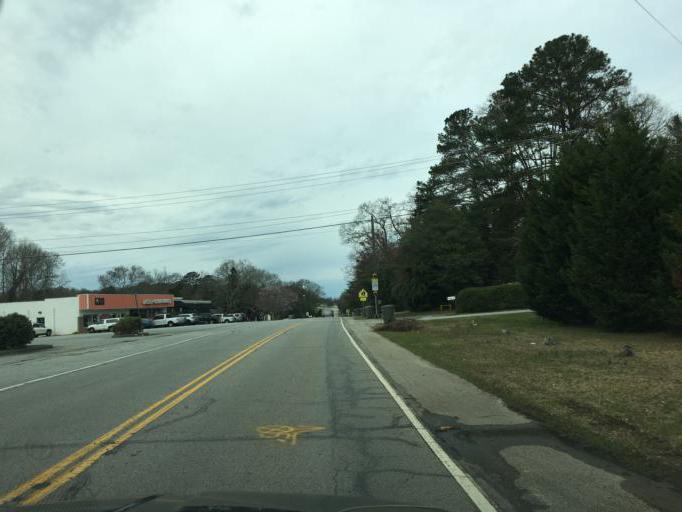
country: US
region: South Carolina
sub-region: Pickens County
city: Clemson
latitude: 34.6726
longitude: -82.8102
